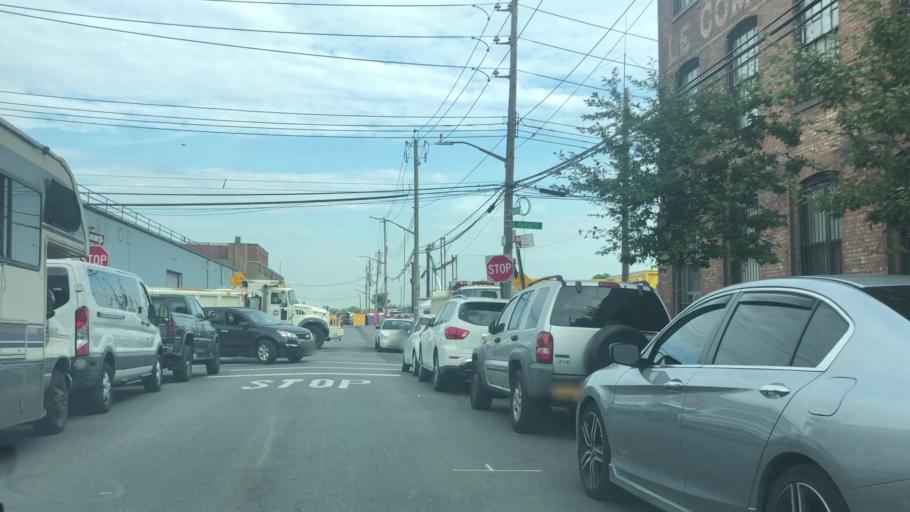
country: US
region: New York
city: New York City
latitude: 40.6790
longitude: -74.0153
